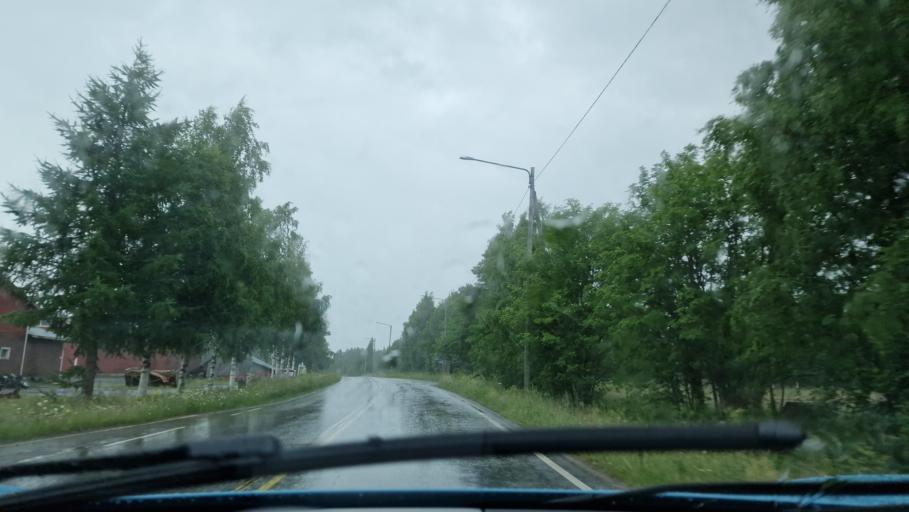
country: FI
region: Southern Ostrobothnia
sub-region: Jaerviseutu
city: Soini
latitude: 62.8420
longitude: 24.3284
